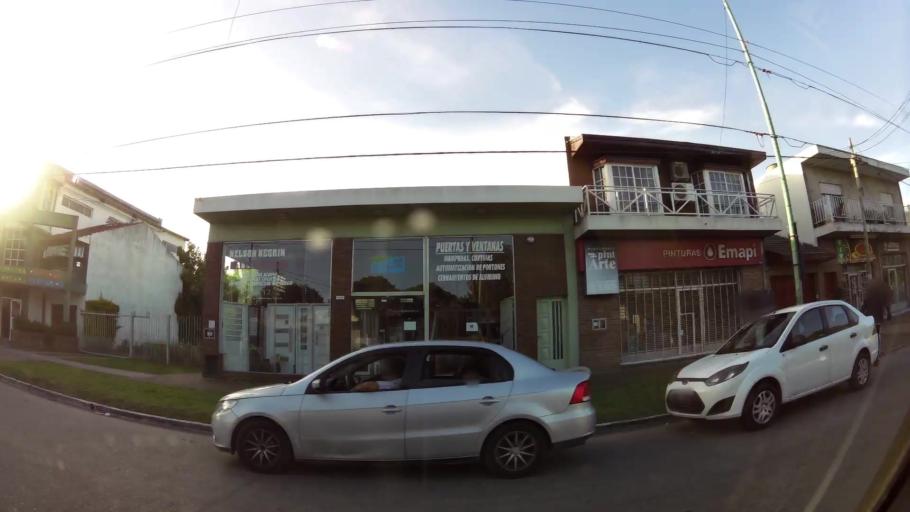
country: AR
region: Buenos Aires
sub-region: Partido de Quilmes
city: Quilmes
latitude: -34.7864
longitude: -58.2112
